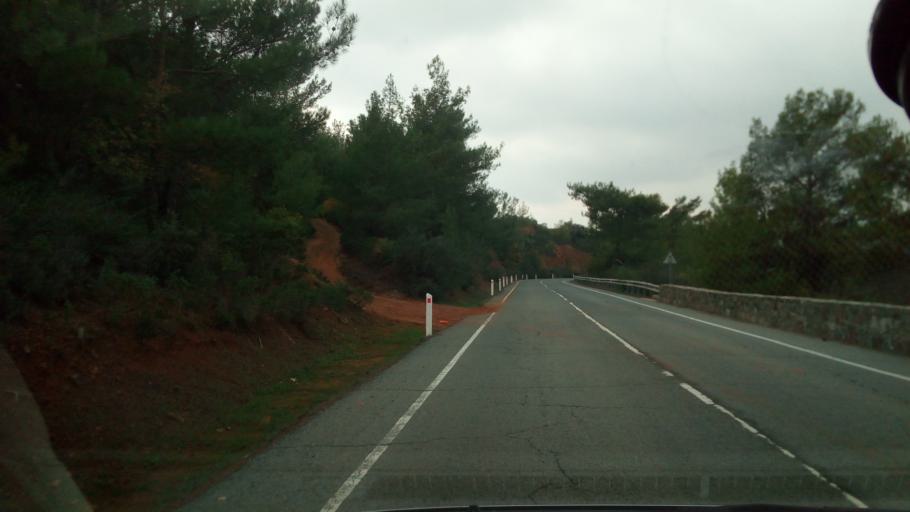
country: CY
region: Lefkosia
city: Lythrodontas
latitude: 34.8773
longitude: 33.2595
